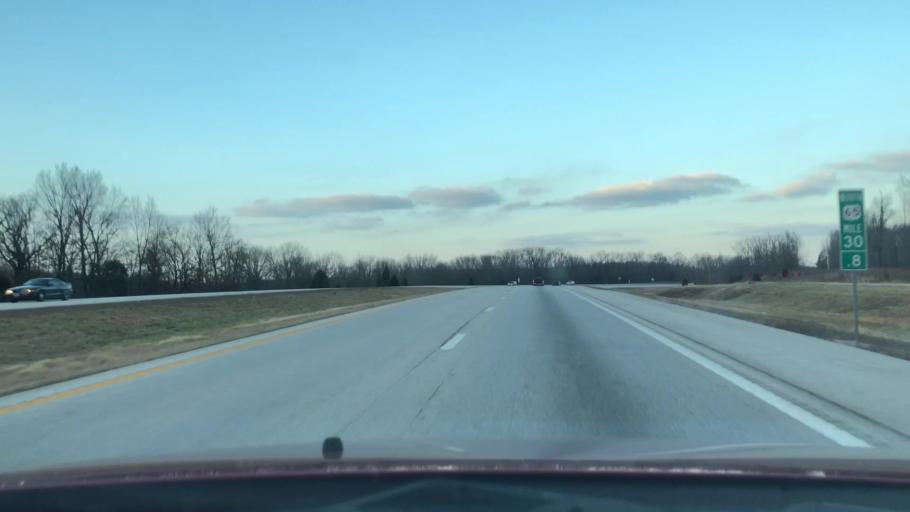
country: US
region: Missouri
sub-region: Christian County
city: Ozark
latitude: 36.9185
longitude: -93.2433
